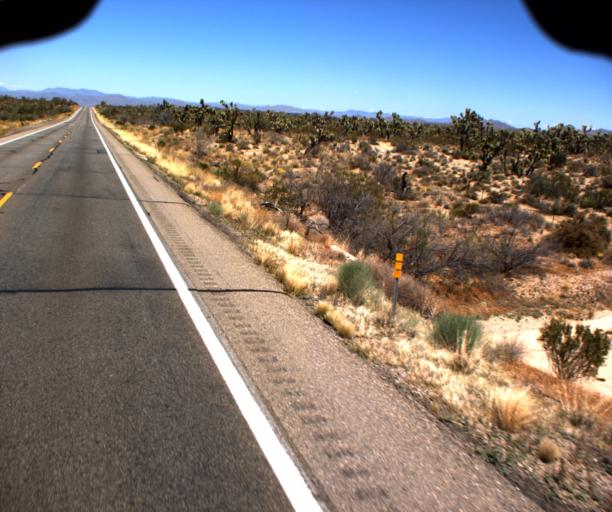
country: US
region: Arizona
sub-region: Yavapai County
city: Congress
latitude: 34.2501
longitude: -113.0817
